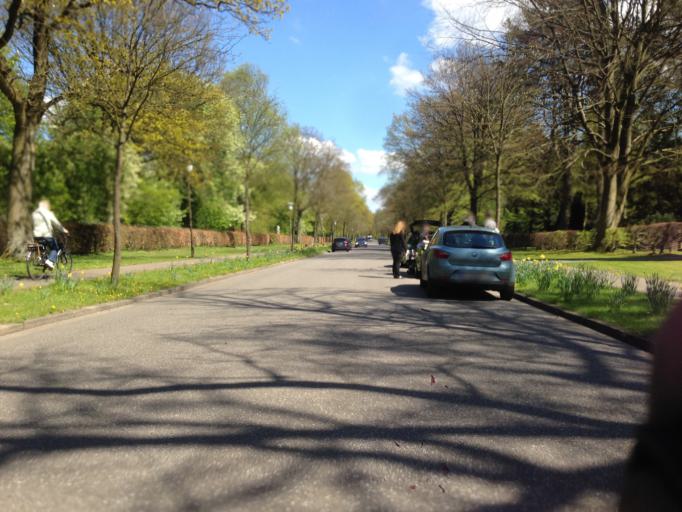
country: DE
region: Hamburg
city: Wellingsbuettel
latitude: 53.6271
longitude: 10.0791
